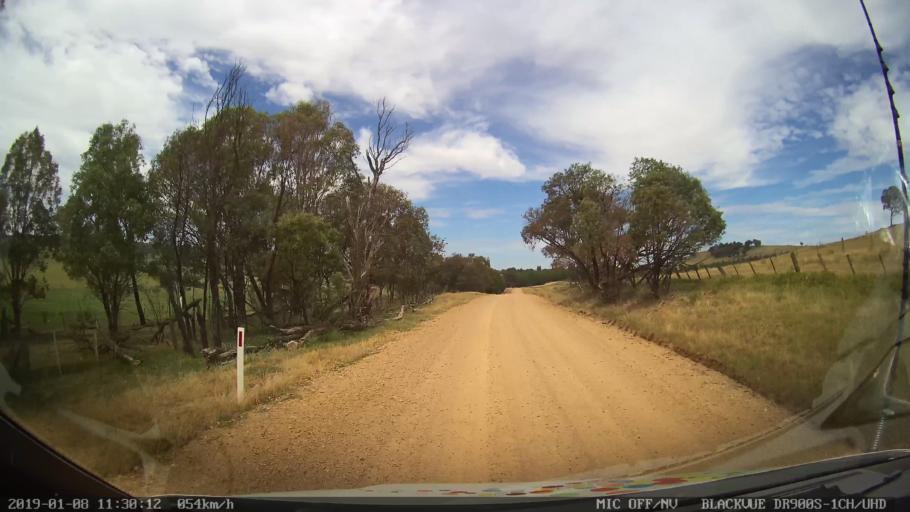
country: AU
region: New South Wales
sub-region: Guyra
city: Guyra
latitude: -30.3060
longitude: 151.5457
